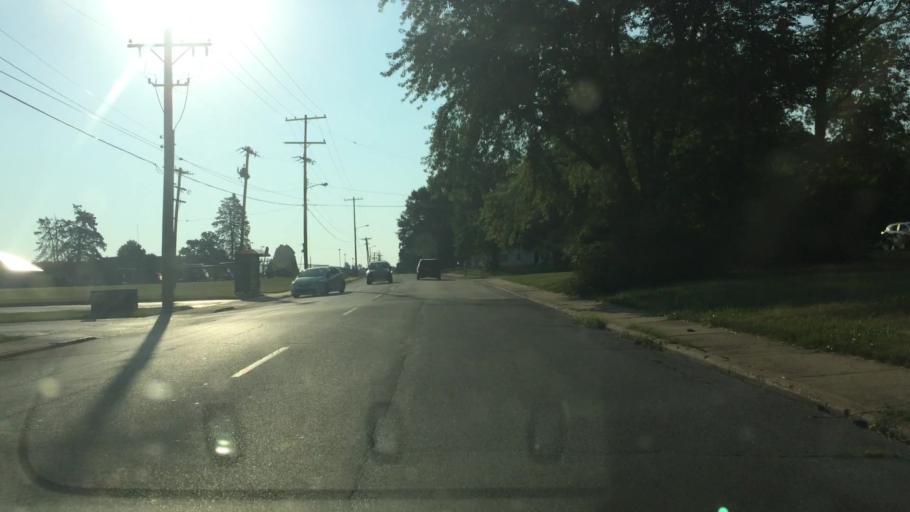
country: US
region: Missouri
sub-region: Greene County
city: Springfield
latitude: 37.2184
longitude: -93.2670
